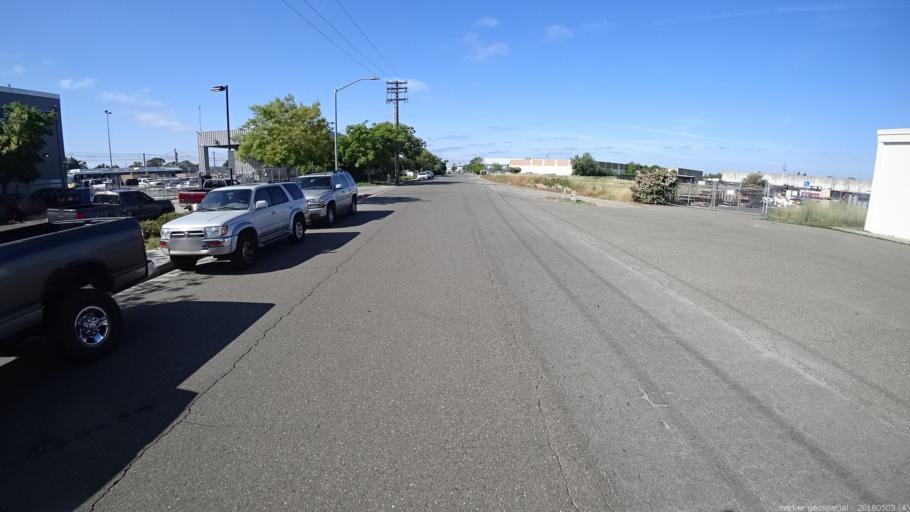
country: US
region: California
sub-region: Sacramento County
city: Arden-Arcade
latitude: 38.6188
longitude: -121.4287
